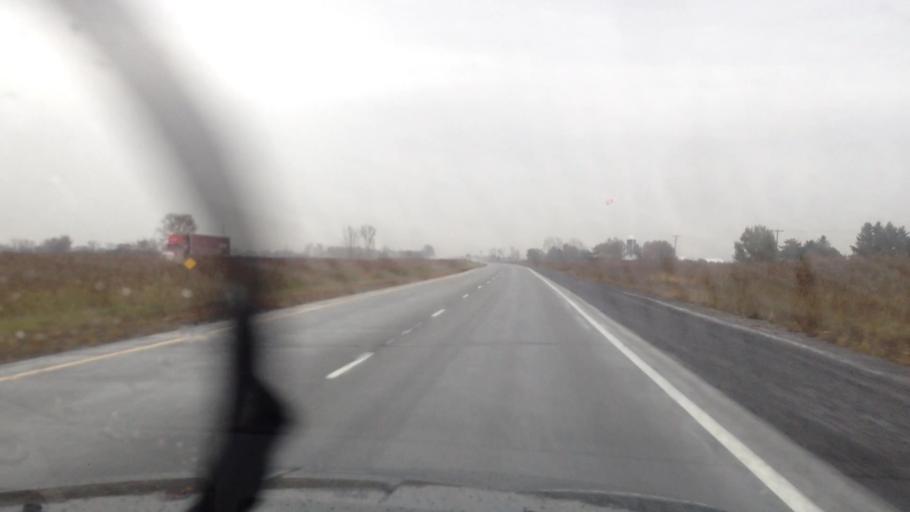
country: CA
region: Ontario
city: Casselman
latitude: 45.3064
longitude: -75.0539
